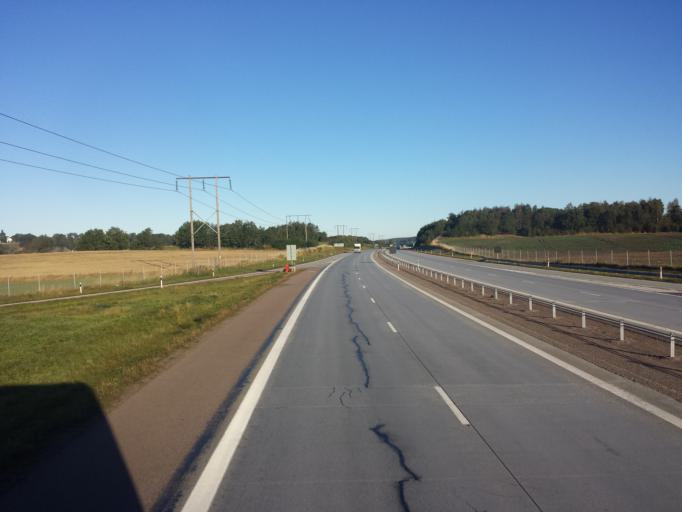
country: SE
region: Halland
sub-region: Halmstads Kommun
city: Getinge
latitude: 56.8518
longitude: 12.6764
